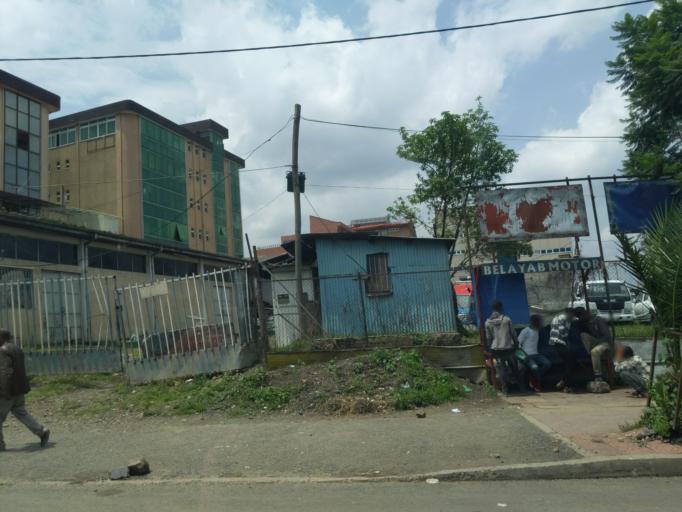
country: ET
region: Adis Abeba
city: Addis Ababa
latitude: 8.9604
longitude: 38.7639
